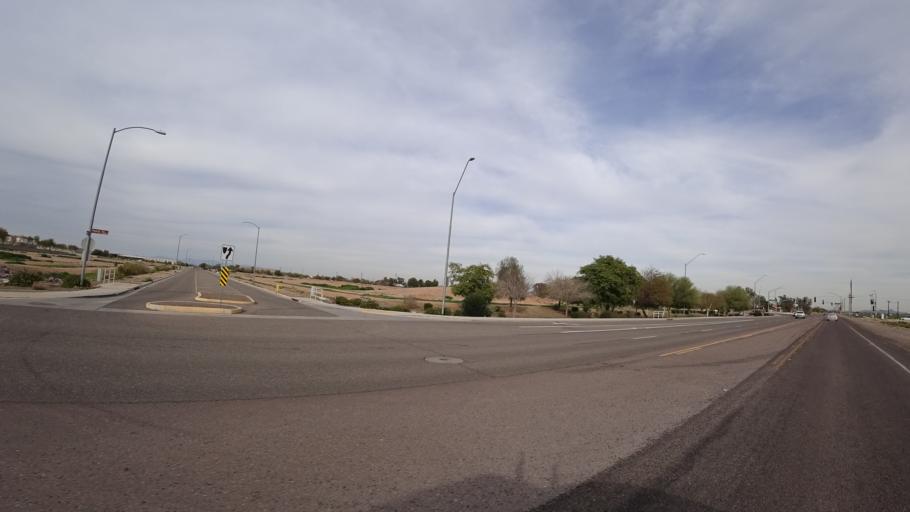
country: US
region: Arizona
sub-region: Maricopa County
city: El Mirage
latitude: 33.5801
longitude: -112.3442
